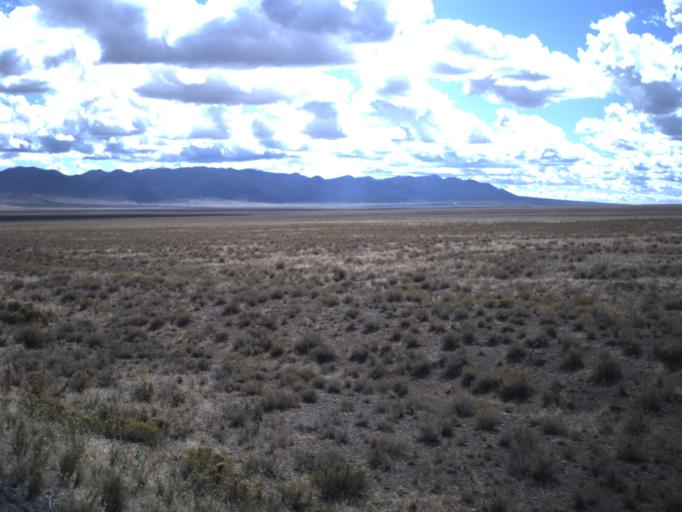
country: US
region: Utah
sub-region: Beaver County
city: Milford
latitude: 38.5604
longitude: -113.7578
